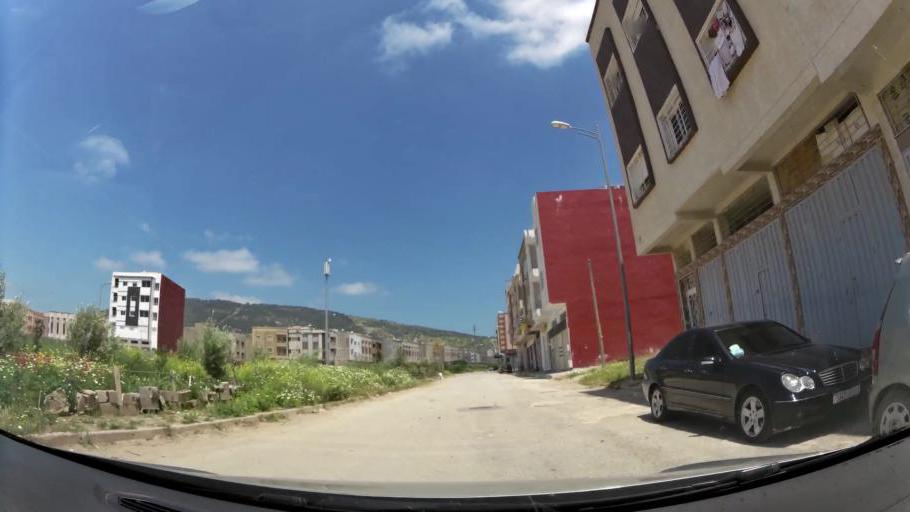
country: MA
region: Fes-Boulemane
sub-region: Fes
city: Fes
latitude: 34.0506
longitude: -5.0441
